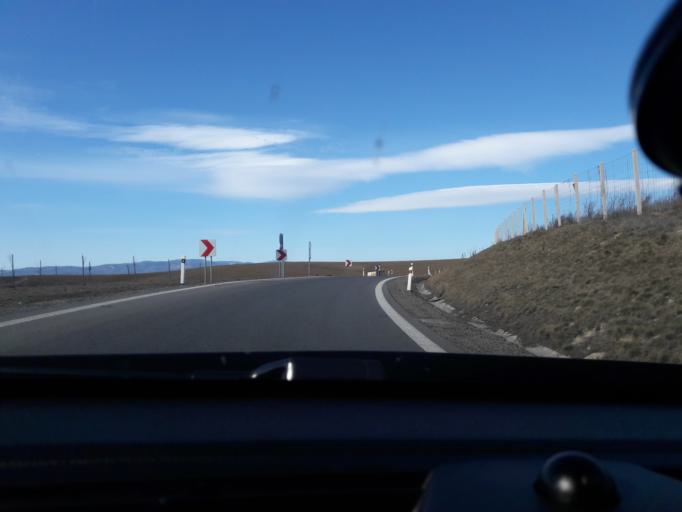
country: SK
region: Banskobystricky
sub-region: Okres Banska Bystrica
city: Zvolen
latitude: 48.5740
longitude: 19.2435
